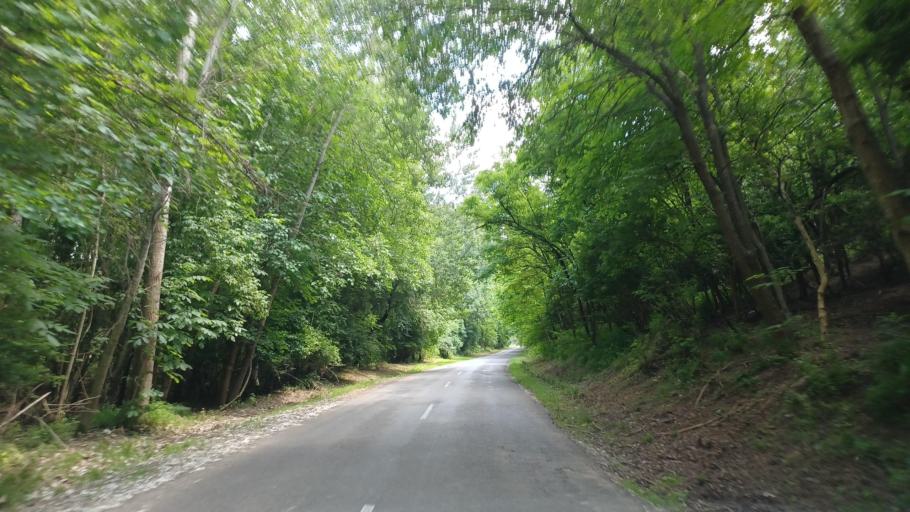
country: HU
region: Tolna
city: Simontornya
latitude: 46.7140
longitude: 18.5043
